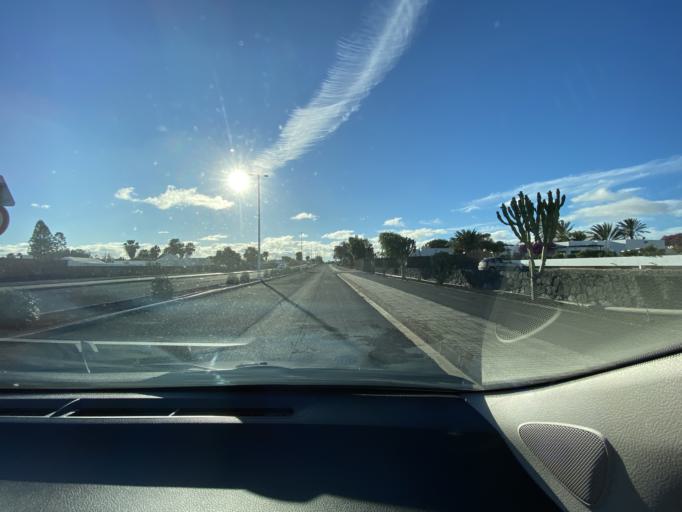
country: ES
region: Canary Islands
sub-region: Provincia de Las Palmas
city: Playa Blanca
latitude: 28.8676
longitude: -13.8346
